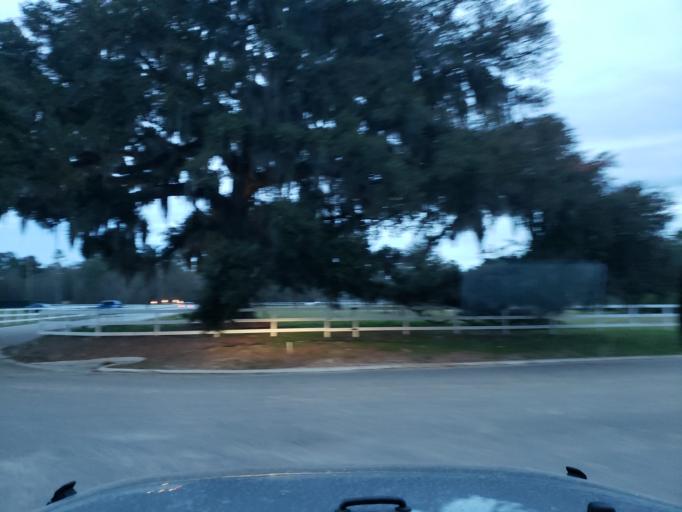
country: US
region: Georgia
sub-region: Bryan County
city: Richmond Hill
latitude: 32.0107
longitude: -81.2972
